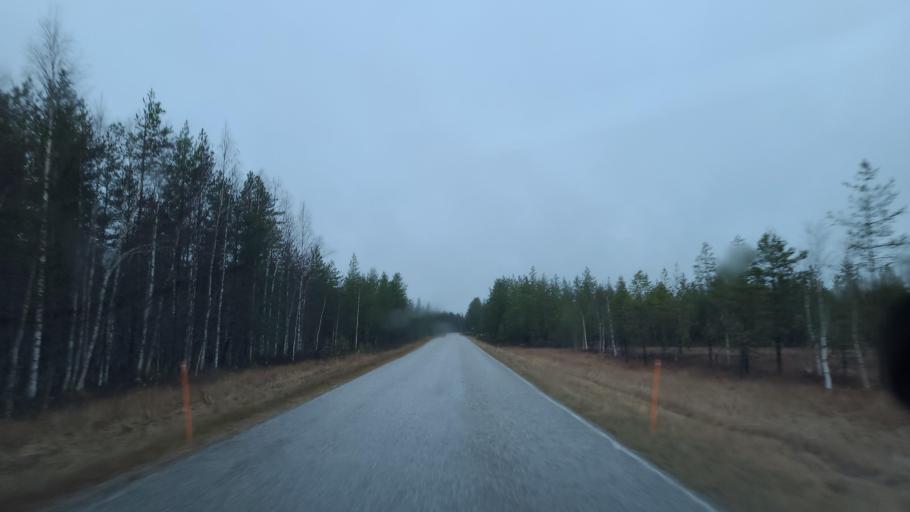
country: FI
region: Lapland
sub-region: Kemi-Tornio
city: Simo
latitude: 65.9146
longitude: 25.2010
